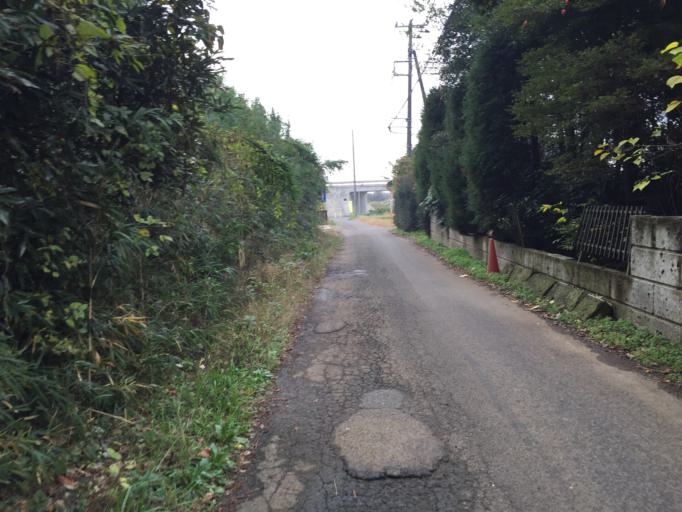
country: JP
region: Ibaraki
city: Naka
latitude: 36.0391
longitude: 140.1503
